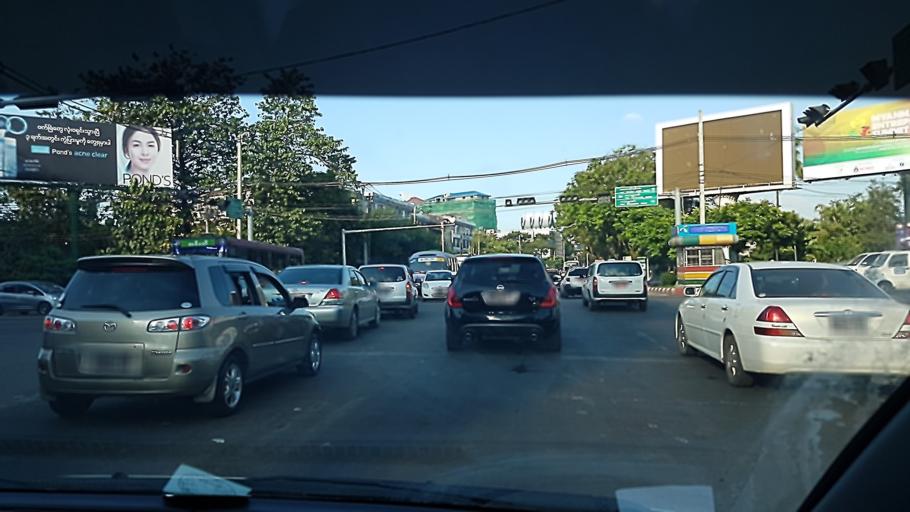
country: MM
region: Yangon
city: Yangon
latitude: 16.8219
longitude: 96.1822
